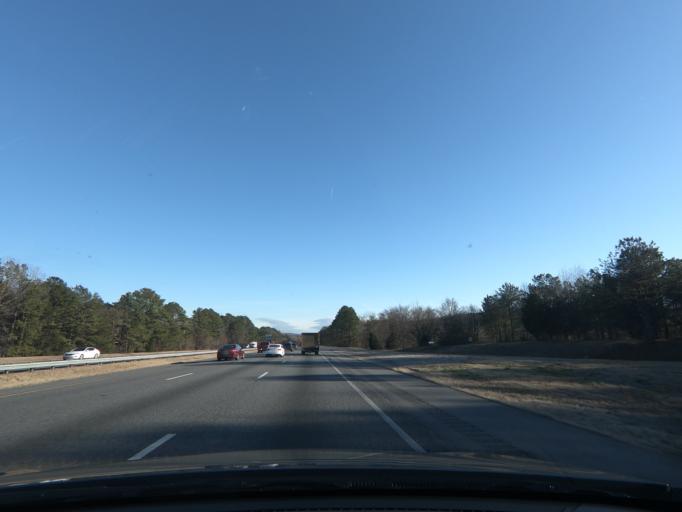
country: US
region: Georgia
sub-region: Bartow County
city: Cartersville
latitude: 34.2711
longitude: -84.8097
